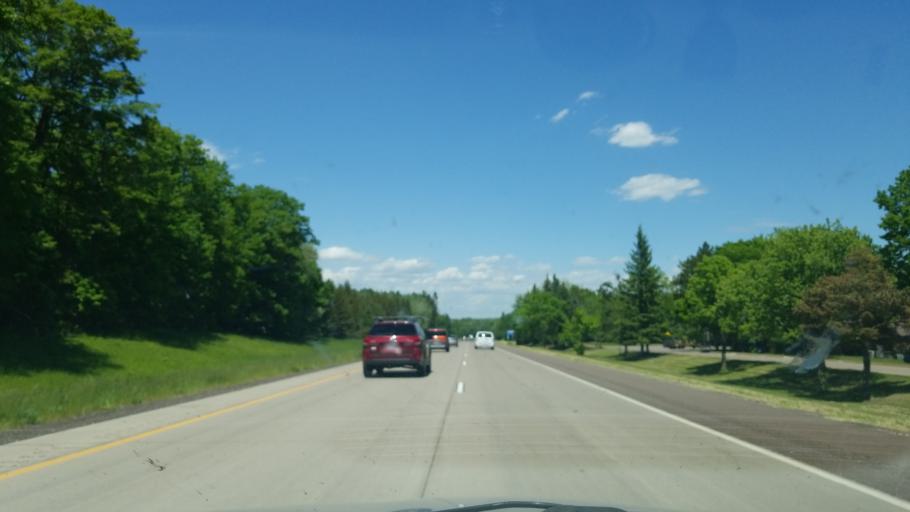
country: US
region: Minnesota
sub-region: Pine County
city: Sandstone
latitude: 46.2107
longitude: -92.8386
